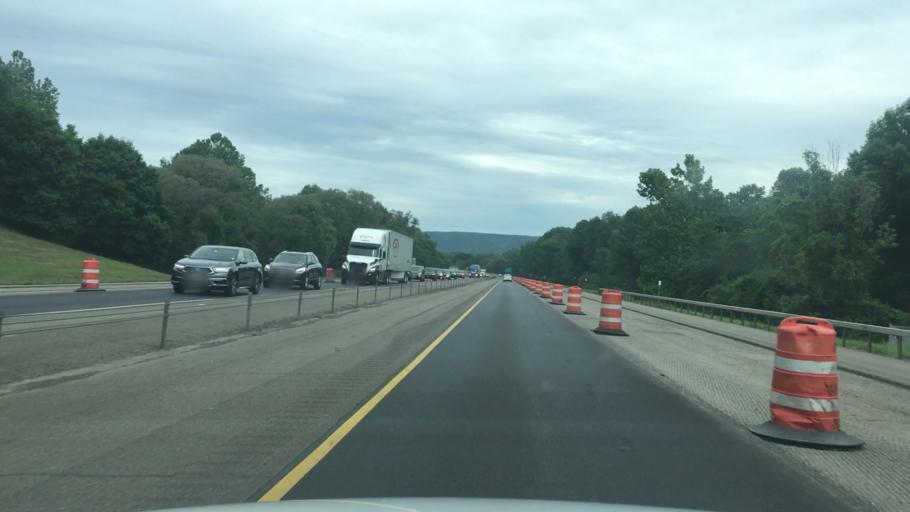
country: US
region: New York
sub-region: Otsego County
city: Oneonta
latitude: 42.4521
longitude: -75.0409
